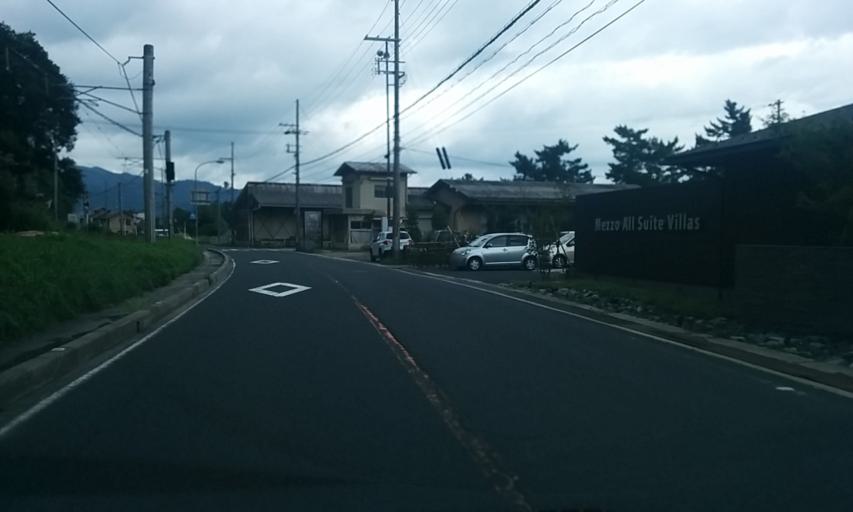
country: JP
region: Kyoto
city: Miyazu
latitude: 35.5490
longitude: 135.1871
